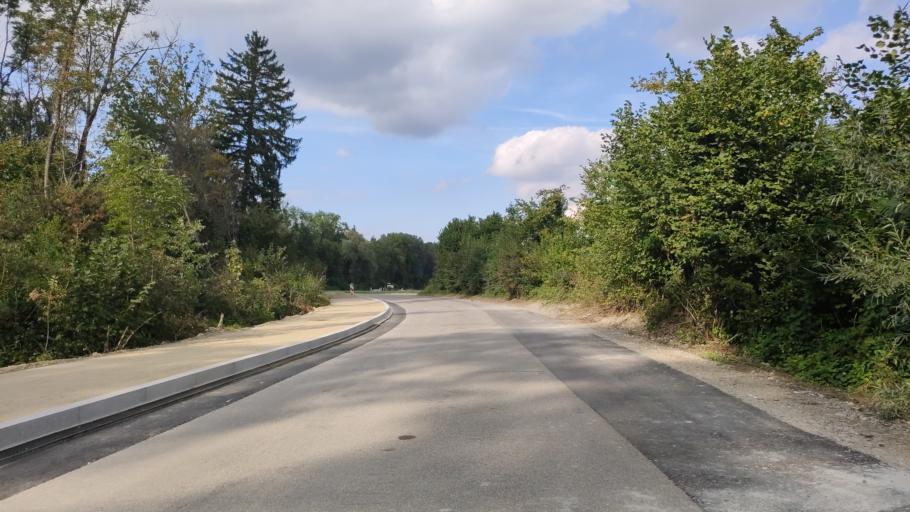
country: DE
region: Bavaria
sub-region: Upper Bavaria
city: Scheuring
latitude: 48.1573
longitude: 10.8790
